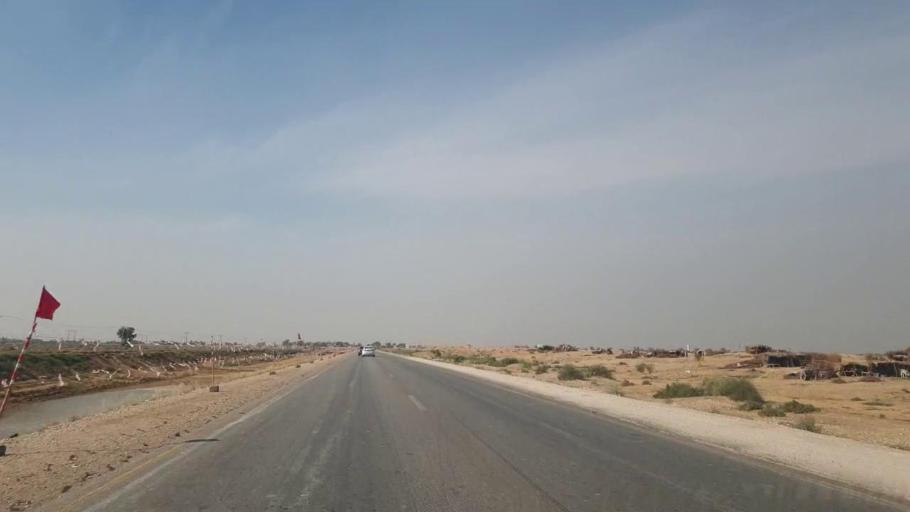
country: PK
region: Sindh
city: Sann
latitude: 26.0220
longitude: 68.1334
